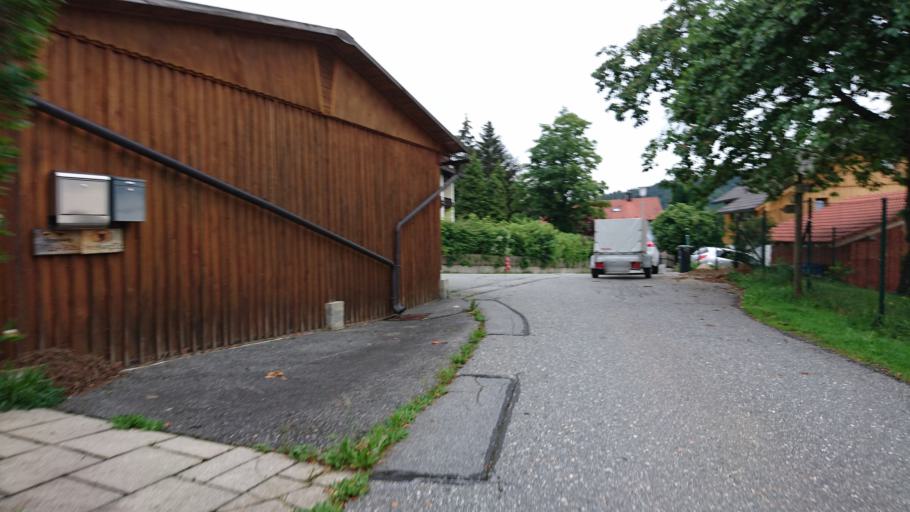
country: DE
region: Bavaria
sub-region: Lower Bavaria
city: Neuschonau
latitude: 48.8818
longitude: 13.4698
